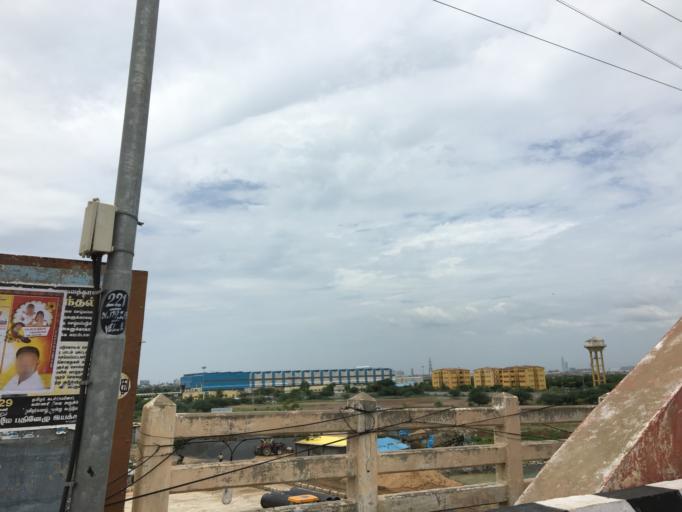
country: IN
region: Tamil Nadu
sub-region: Kancheepuram
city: Madipakkam
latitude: 12.9675
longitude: 80.2177
